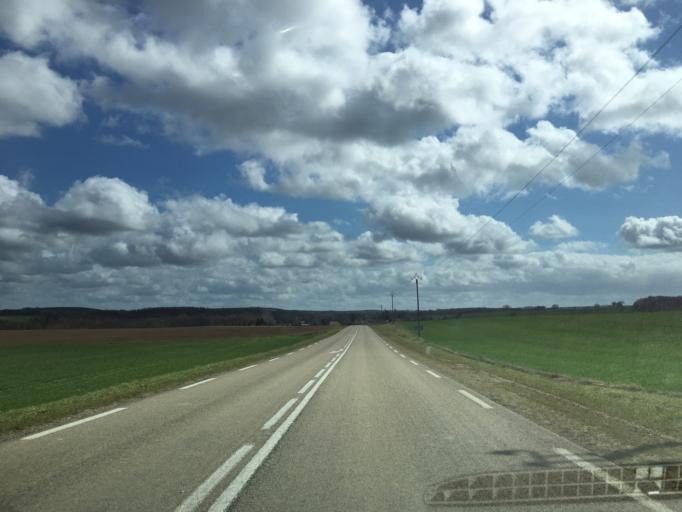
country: FR
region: Bourgogne
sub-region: Departement de l'Yonne
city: Aillant-sur-Tholon
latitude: 47.8486
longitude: 3.3831
